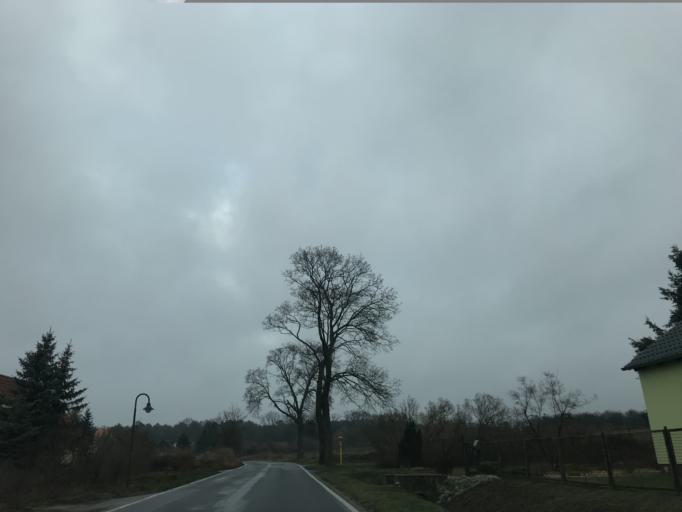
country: DE
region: Brandenburg
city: Brieselang
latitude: 52.6736
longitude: 12.9741
